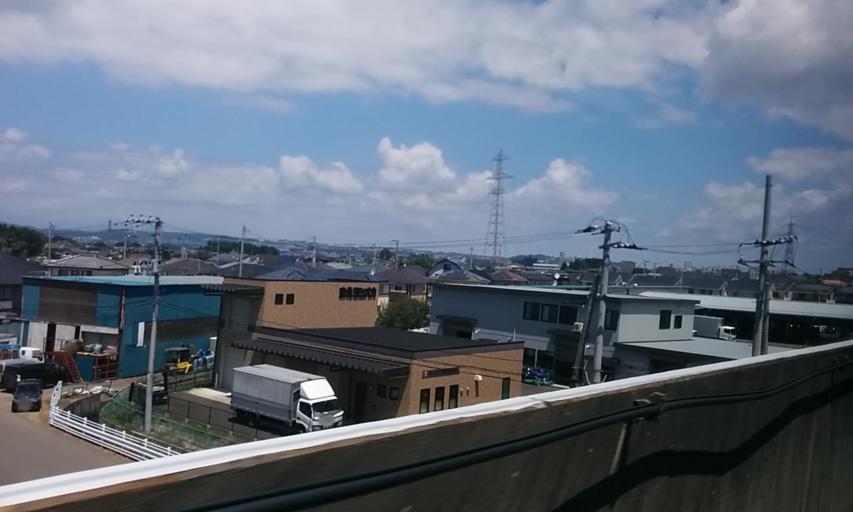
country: JP
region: Miyagi
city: Iwanuma
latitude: 38.1794
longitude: 140.8717
